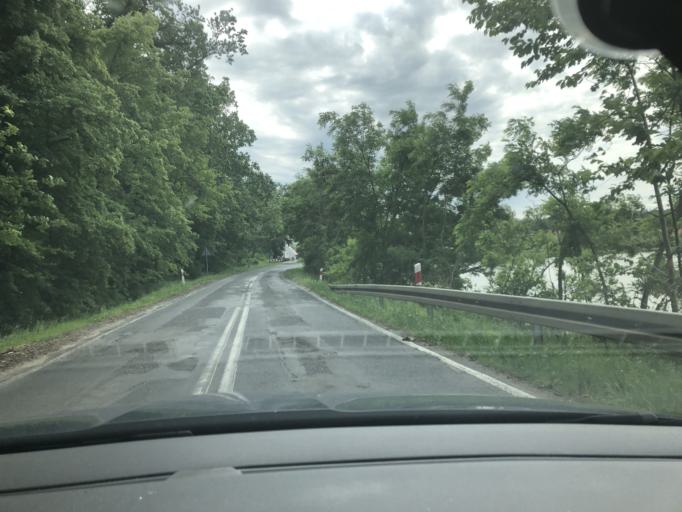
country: PL
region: Lower Silesian Voivodeship
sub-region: Powiat zlotoryjski
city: Zlotoryja
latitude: 51.1419
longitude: 15.9235
